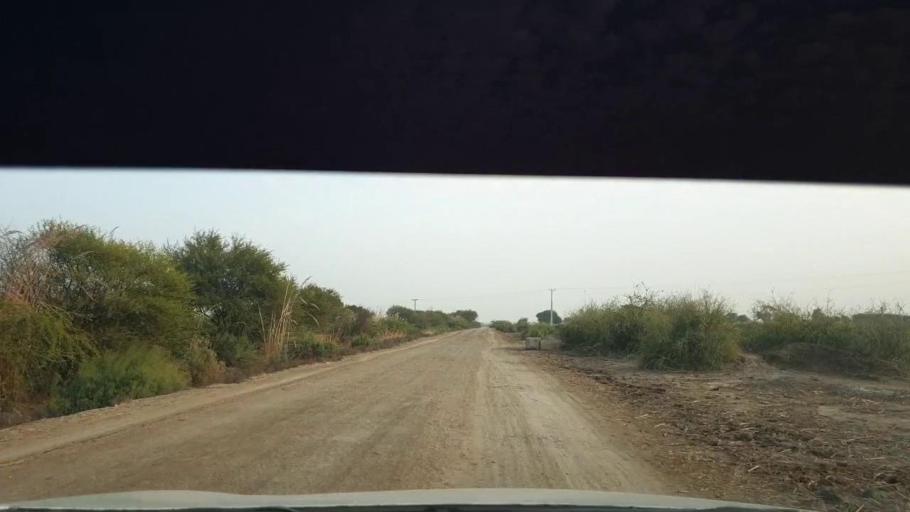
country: PK
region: Sindh
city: Berani
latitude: 25.7234
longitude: 68.9777
